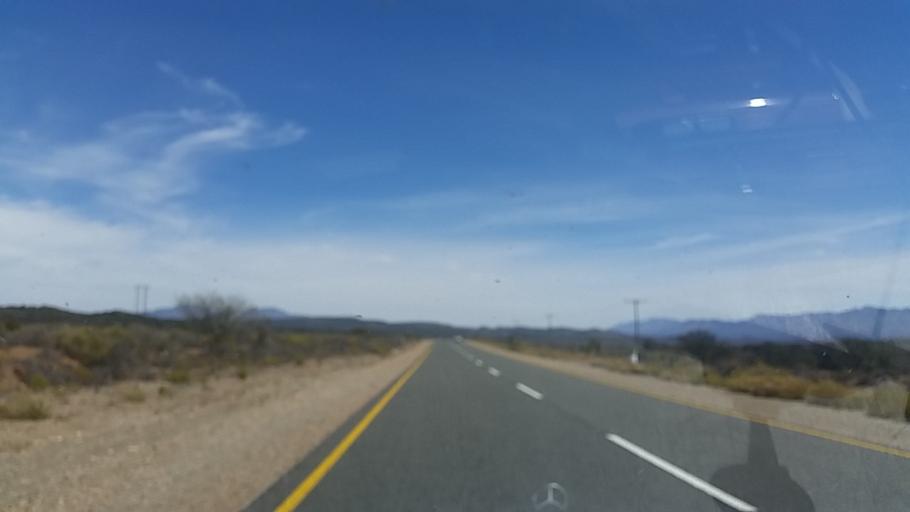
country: ZA
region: Eastern Cape
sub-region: Cacadu District Municipality
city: Willowmore
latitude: -33.5017
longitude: 23.2532
